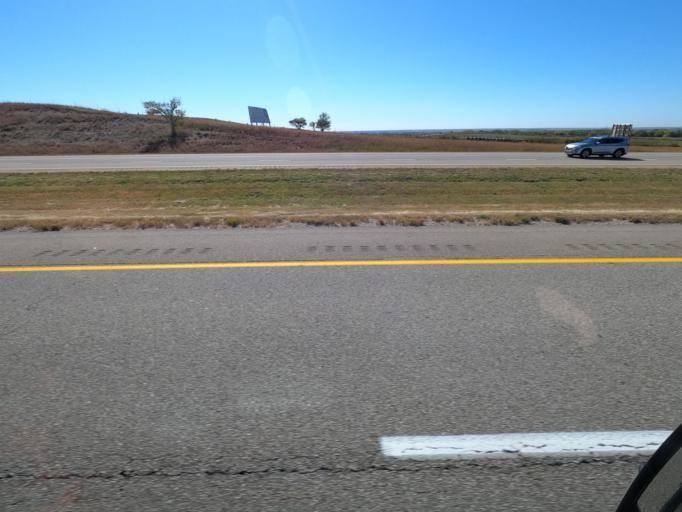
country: US
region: Kansas
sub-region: Ellsworth County
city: Ellsworth
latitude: 38.8489
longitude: -98.5099
